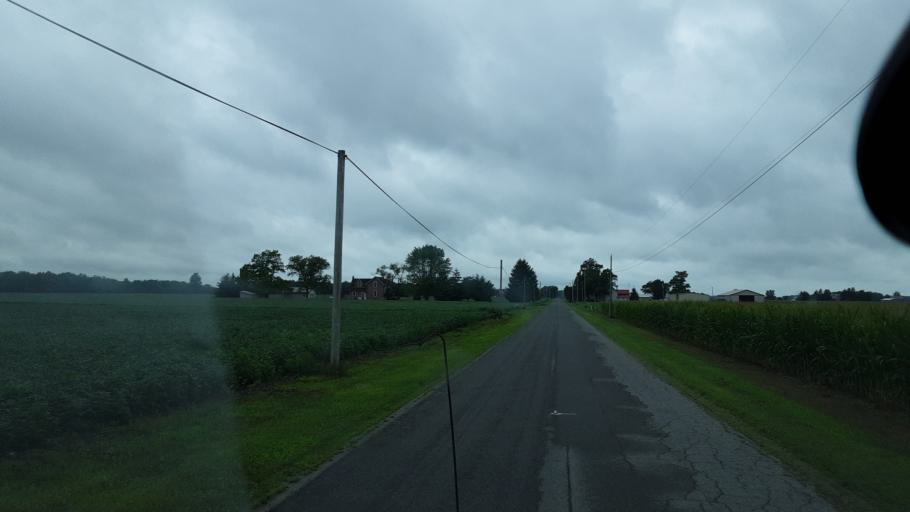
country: US
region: Ohio
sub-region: Van Wert County
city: Convoy
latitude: 40.8224
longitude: -84.7203
